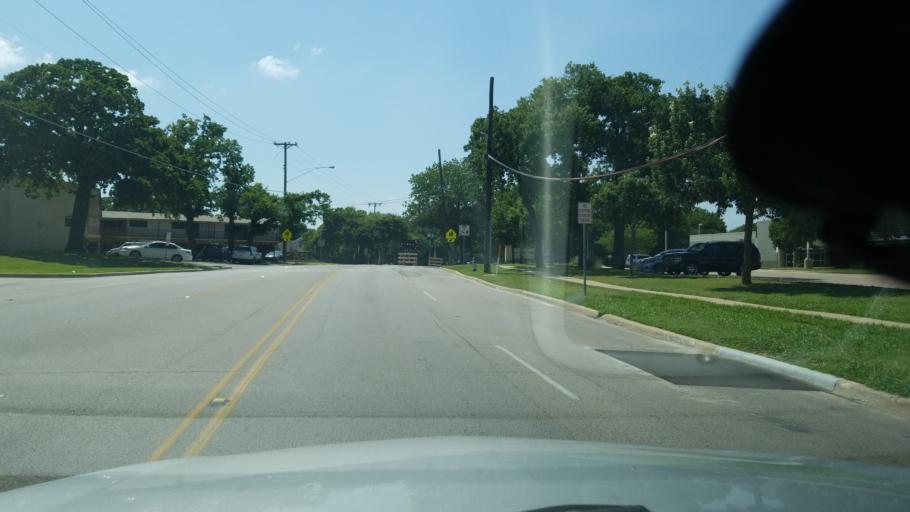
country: US
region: Texas
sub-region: Dallas County
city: Irving
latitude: 32.8187
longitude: -96.9540
